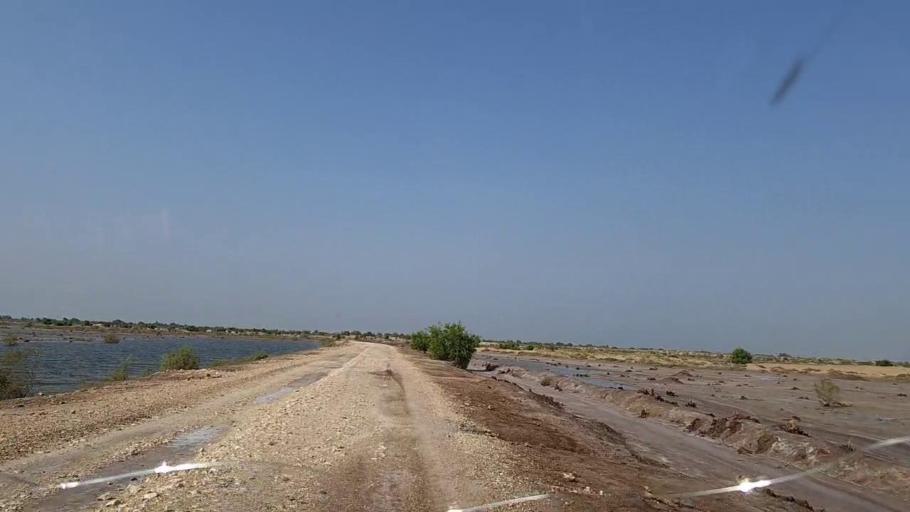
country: PK
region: Sindh
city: Khanpur
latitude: 27.6933
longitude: 69.3835
